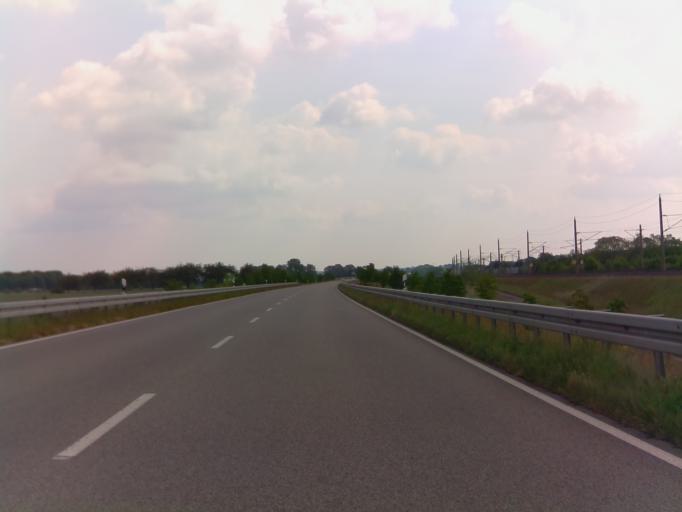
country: DE
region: Saxony-Anhalt
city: Uchtspringe
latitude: 52.5583
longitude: 11.6289
